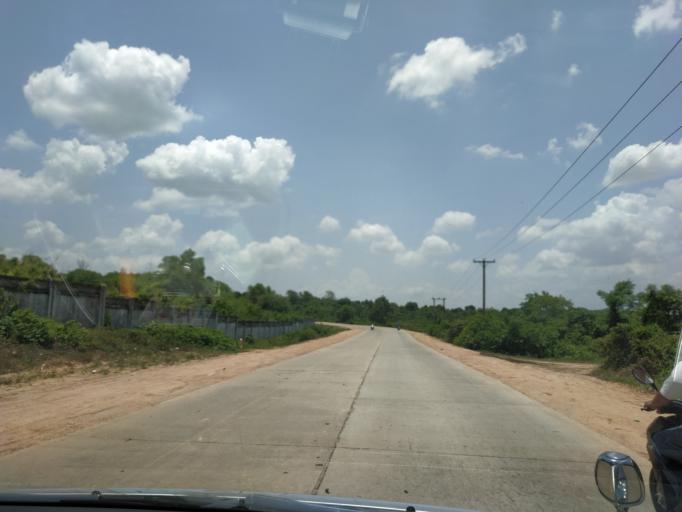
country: MM
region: Bago
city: Bago
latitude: 17.4675
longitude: 96.4620
